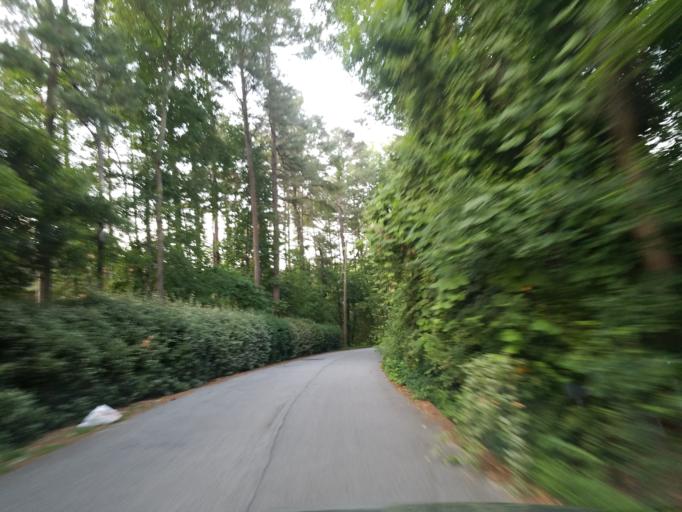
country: US
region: Georgia
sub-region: Cobb County
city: Vinings
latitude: 33.8682
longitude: -84.4649
